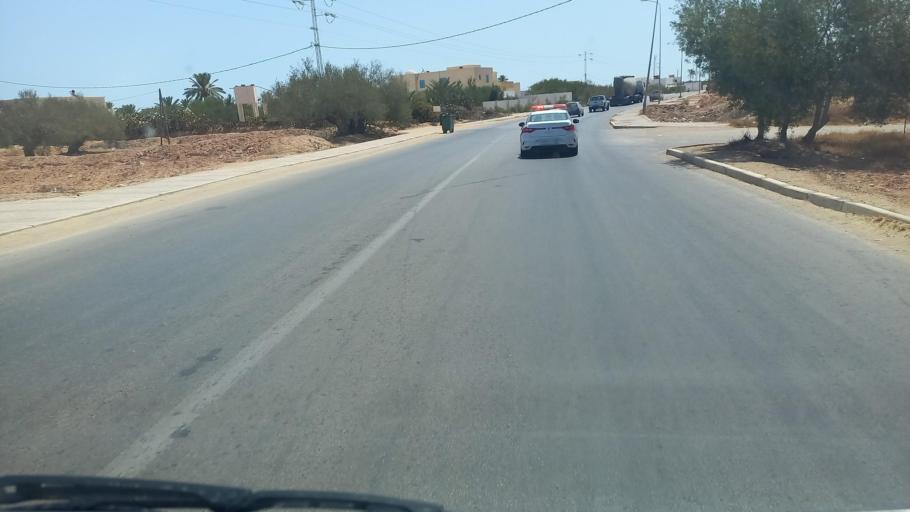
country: TN
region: Madanin
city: Houmt Souk
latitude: 33.7806
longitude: 10.8903
